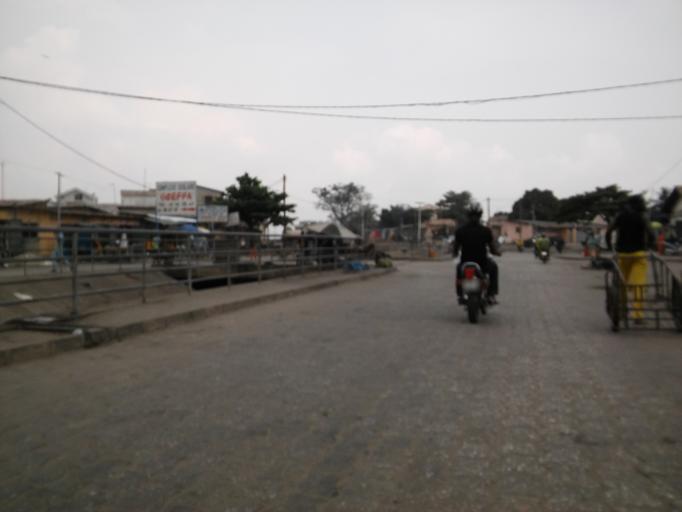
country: BJ
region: Littoral
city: Cotonou
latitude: 6.3841
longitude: 2.4242
